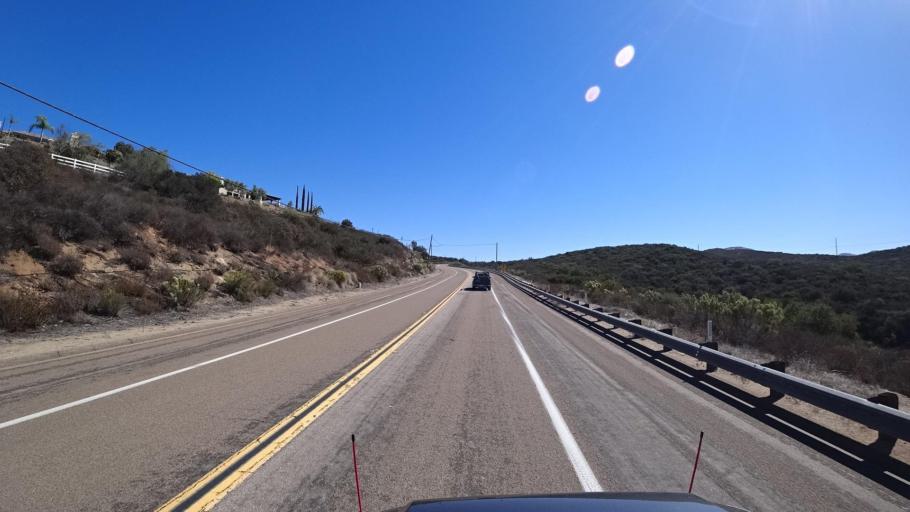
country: US
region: California
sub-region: San Diego County
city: Alpine
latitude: 32.8031
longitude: -116.7747
